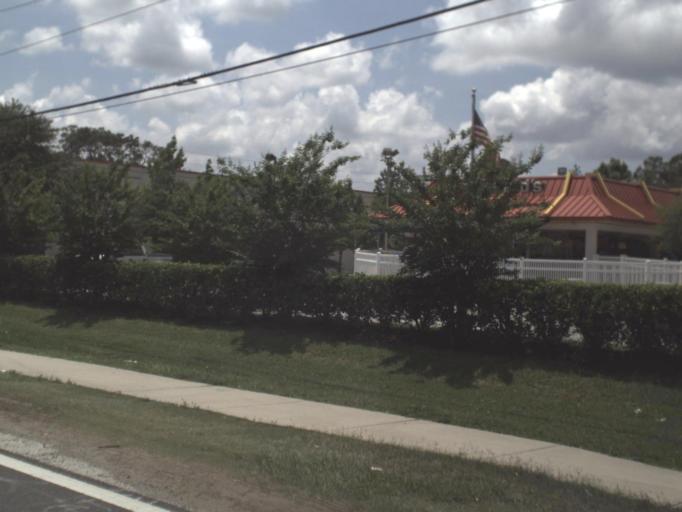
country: US
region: Florida
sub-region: Clay County
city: Bellair-Meadowbrook Terrace
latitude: 30.2055
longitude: -81.7396
